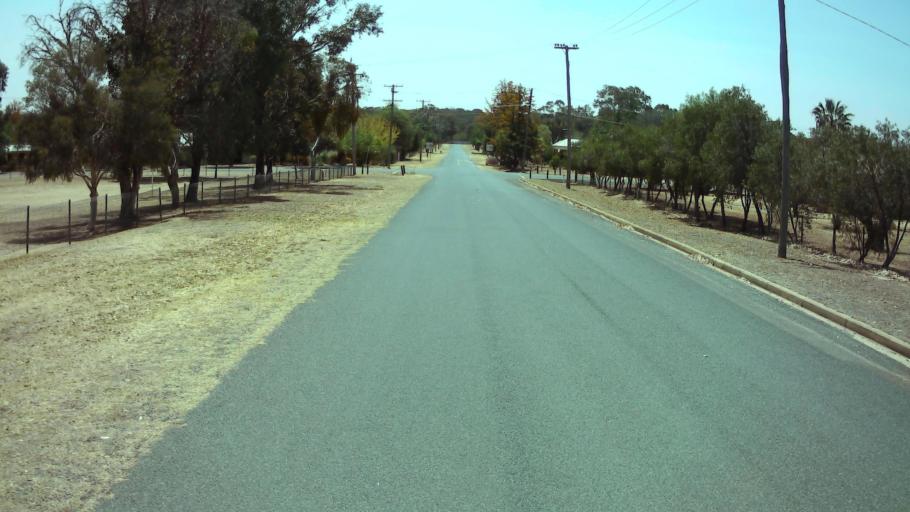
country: AU
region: New South Wales
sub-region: Weddin
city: Grenfell
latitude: -33.8923
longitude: 148.1687
